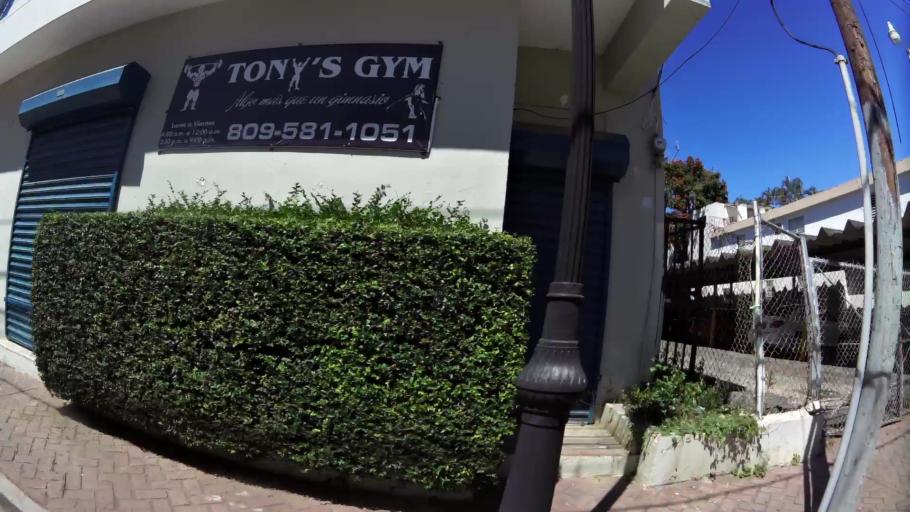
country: DO
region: Santiago
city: Santiago de los Caballeros
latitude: 19.4499
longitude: -70.7008
